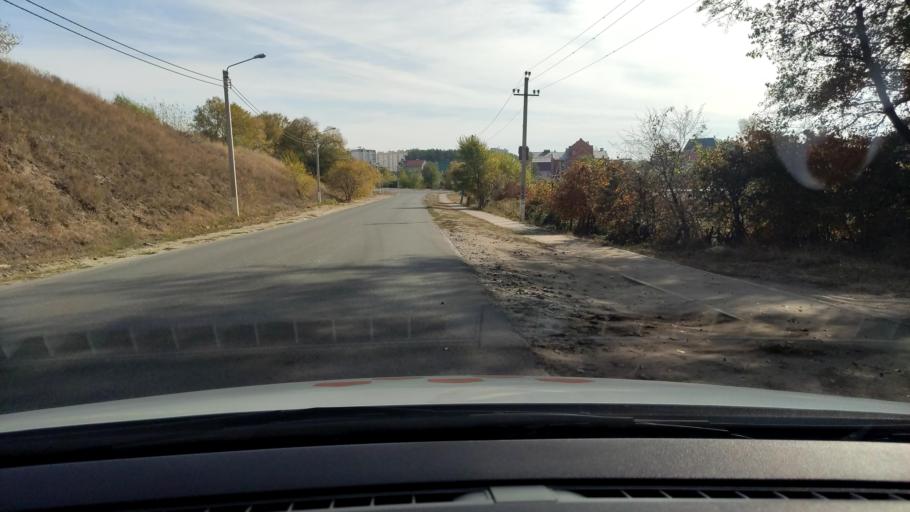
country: RU
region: Voronezj
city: Pridonskoy
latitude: 51.6639
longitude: 39.0894
